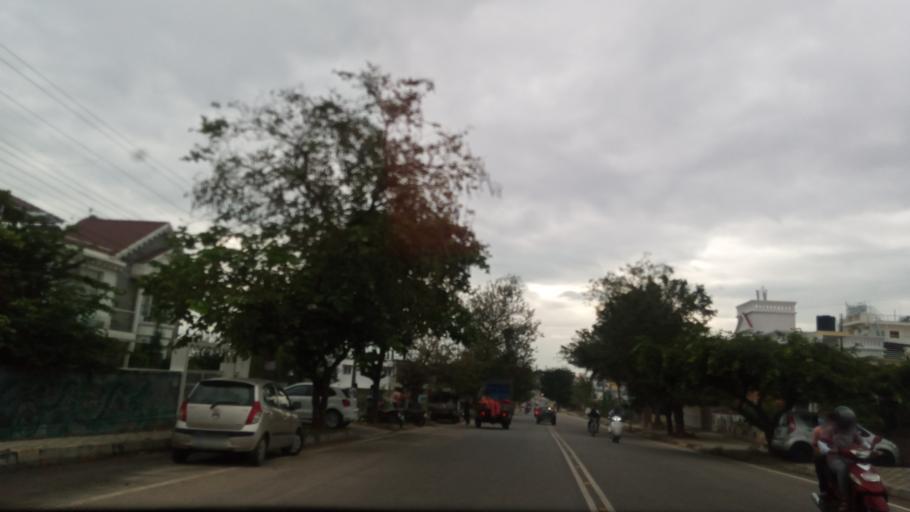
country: IN
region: Karnataka
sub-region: Mysore
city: Mysore
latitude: 12.2953
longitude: 76.6096
